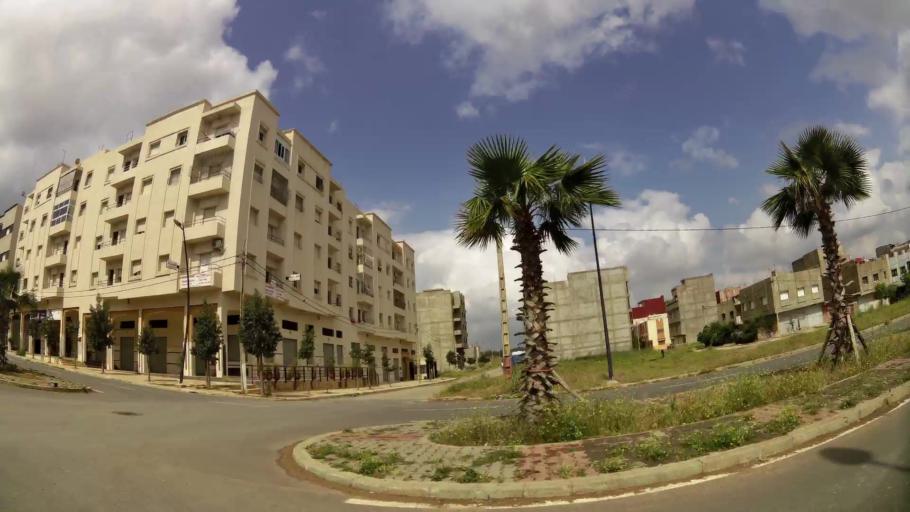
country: MA
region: Rabat-Sale-Zemmour-Zaer
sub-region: Khemisset
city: Tiflet
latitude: 33.8971
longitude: -6.3386
